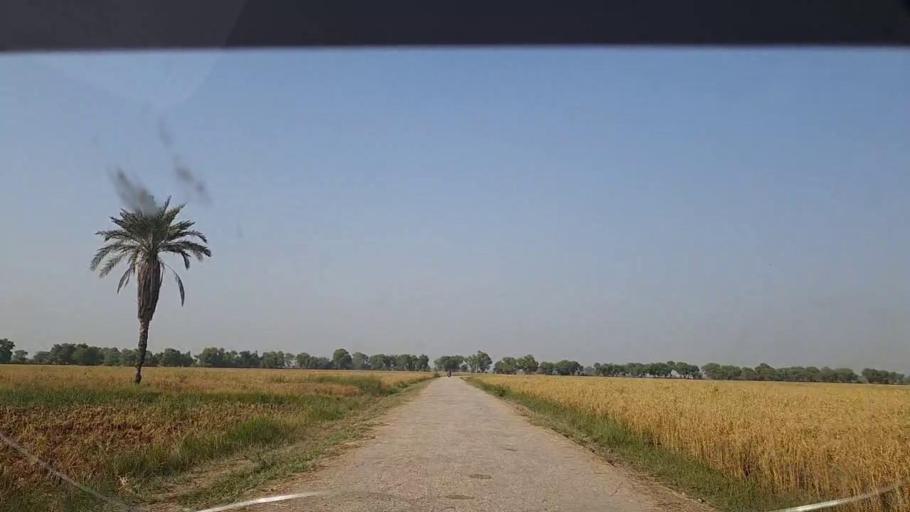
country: PK
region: Sindh
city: Shikarpur
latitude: 28.1199
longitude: 68.5833
